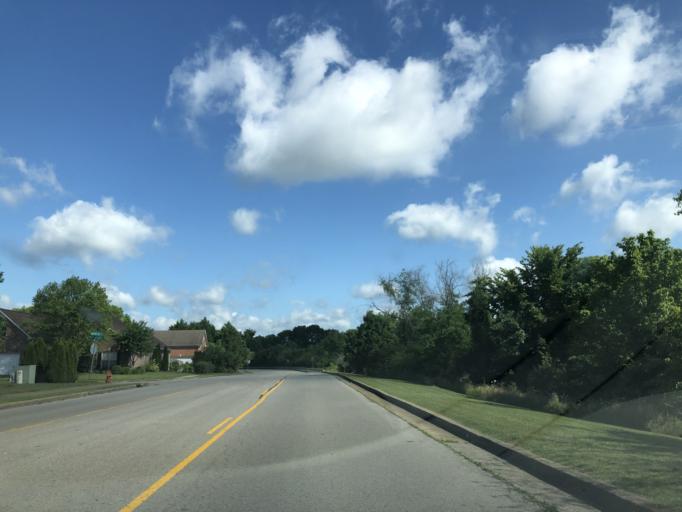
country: US
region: Tennessee
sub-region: Davidson County
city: Belle Meade
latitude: 36.0603
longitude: -86.9488
